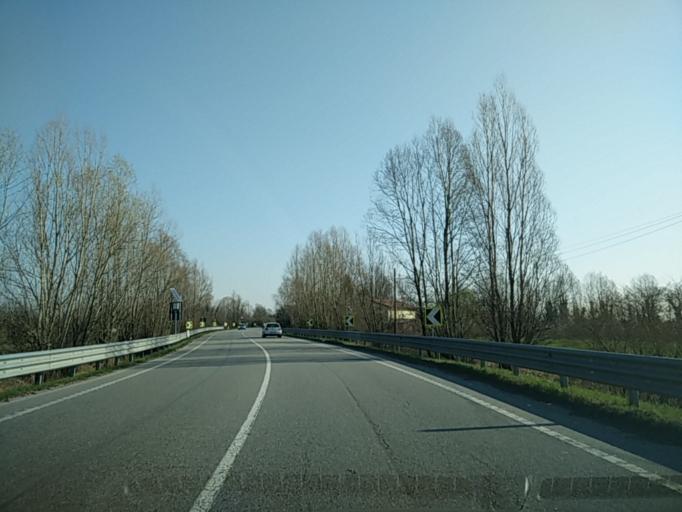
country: IT
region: Friuli Venezia Giulia
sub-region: Provincia di Pordenone
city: Sesto al Reghena
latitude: 45.8876
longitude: 12.8042
